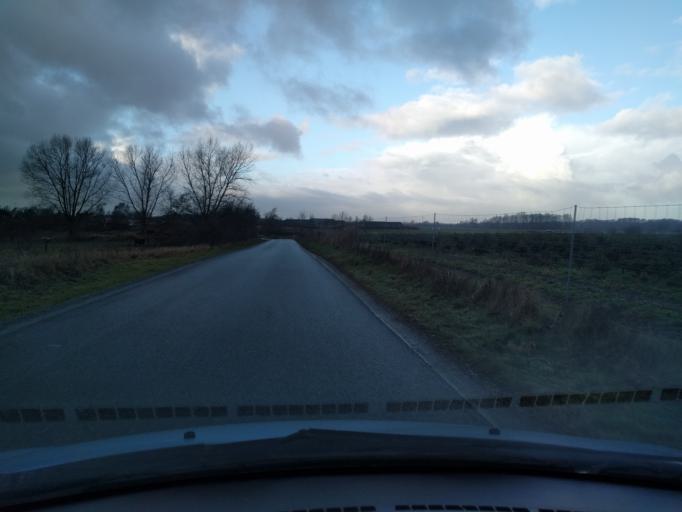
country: DK
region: South Denmark
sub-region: Kerteminde Kommune
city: Langeskov
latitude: 55.3787
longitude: 10.5787
